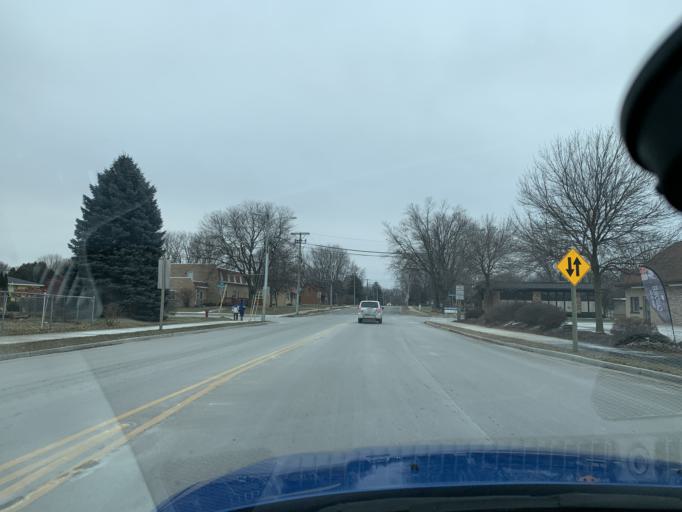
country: US
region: Wisconsin
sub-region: Dane County
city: Sun Prairie
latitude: 43.1962
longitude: -89.2109
